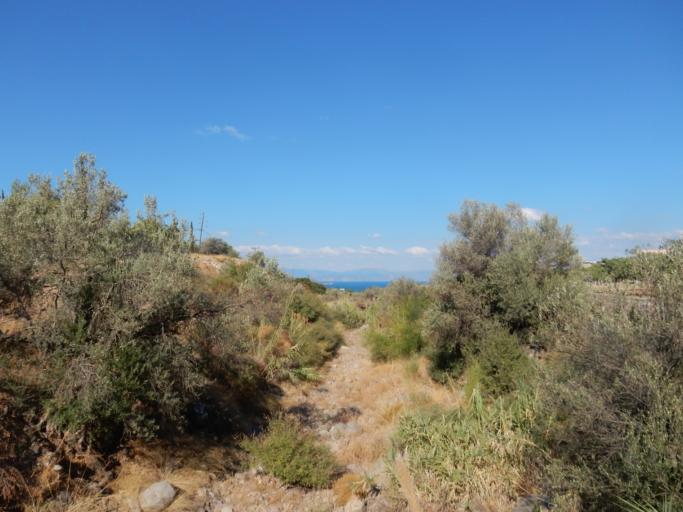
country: GR
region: Attica
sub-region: Nomos Piraios
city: Kypseli
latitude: 37.7345
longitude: 23.4575
